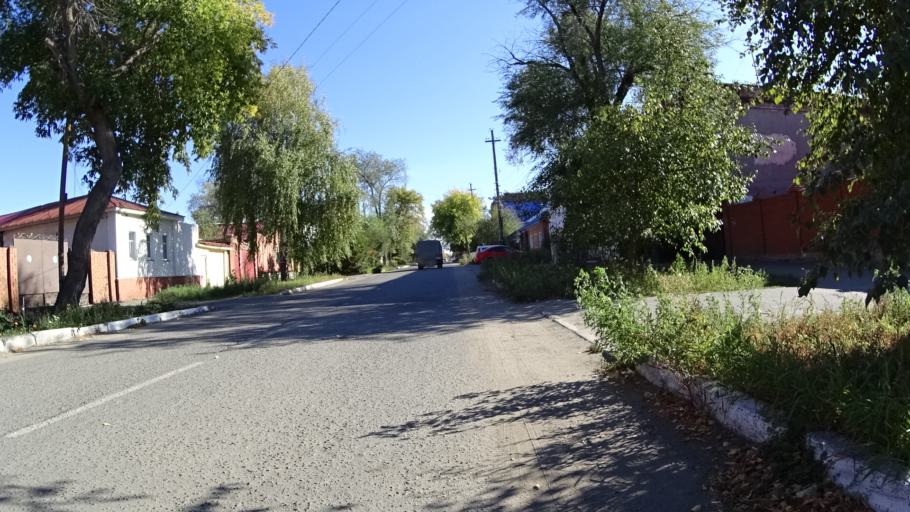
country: RU
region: Chelyabinsk
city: Troitsk
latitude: 54.0838
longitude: 61.5547
